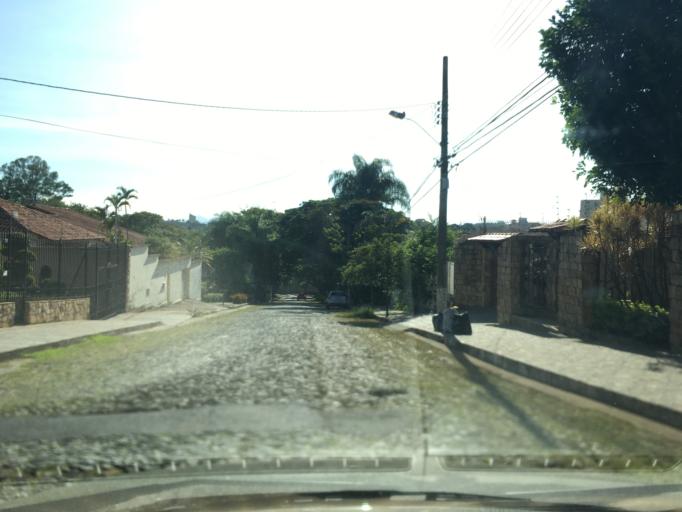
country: BR
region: Minas Gerais
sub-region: Belo Horizonte
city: Belo Horizonte
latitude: -19.8648
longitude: -43.9869
